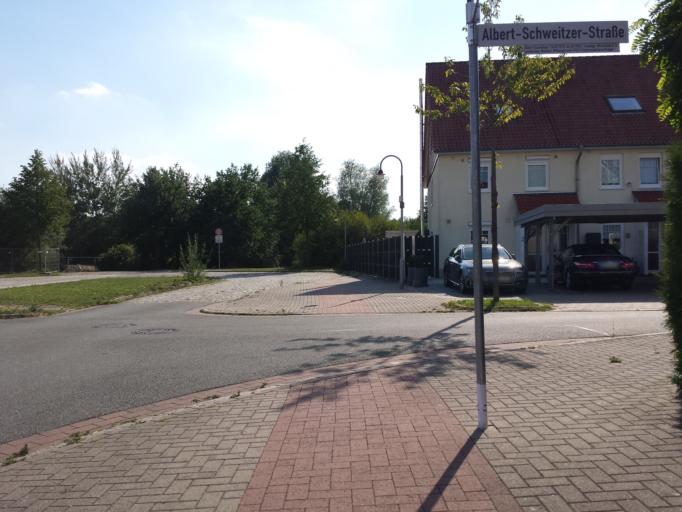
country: DE
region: Bremen
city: Bremen
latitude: 53.0281
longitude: 8.8300
